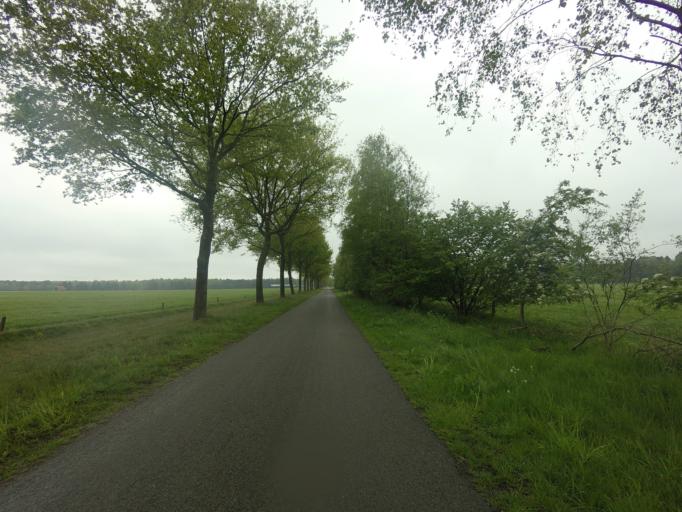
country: DE
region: North Rhine-Westphalia
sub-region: Regierungsbezirk Munster
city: Vreden
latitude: 52.1246
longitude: 6.8292
